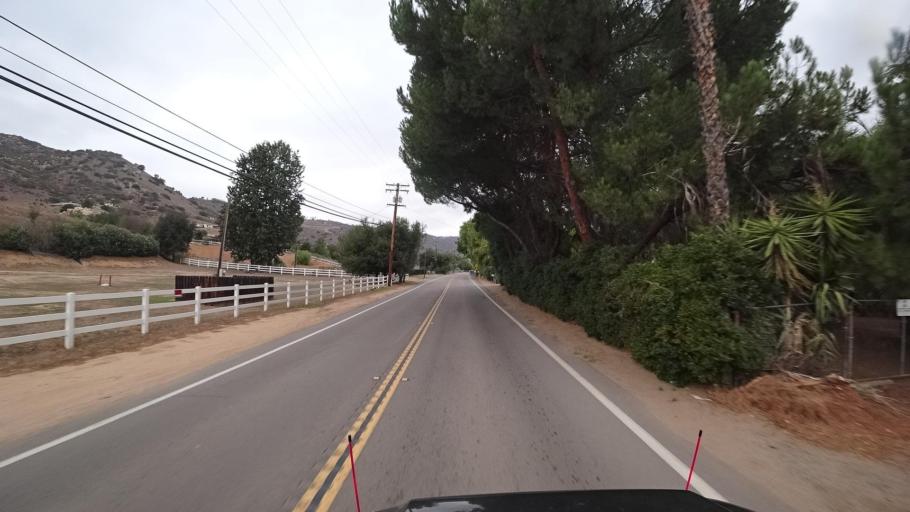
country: US
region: California
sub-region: San Diego County
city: Crest
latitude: 32.7926
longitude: -116.8460
